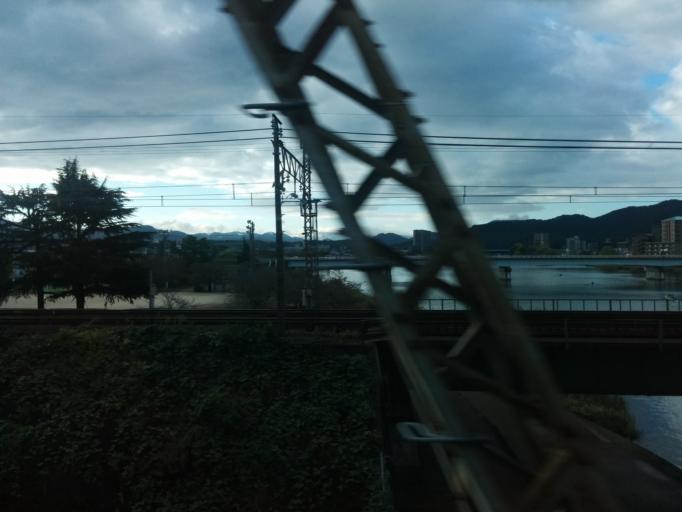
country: JP
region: Shiga Prefecture
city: Otsu-shi
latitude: 34.9801
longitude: 135.9074
